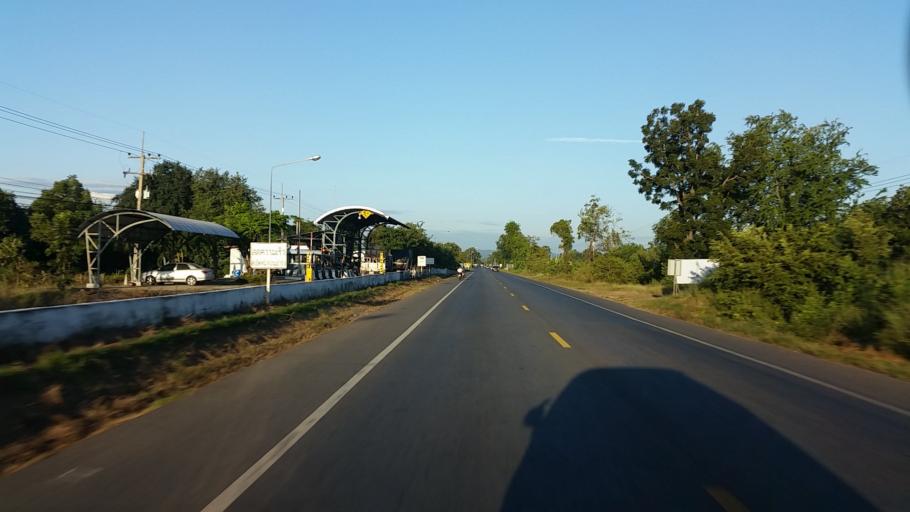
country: TH
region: Lop Buri
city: Chai Badan
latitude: 15.2632
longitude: 101.2082
